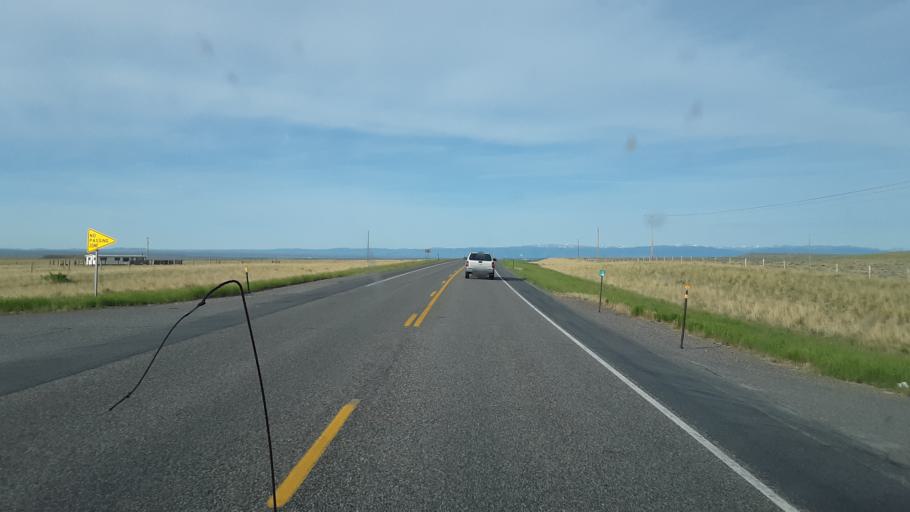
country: US
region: Wyoming
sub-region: Fremont County
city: Riverton
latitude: 43.1531
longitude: -108.2766
